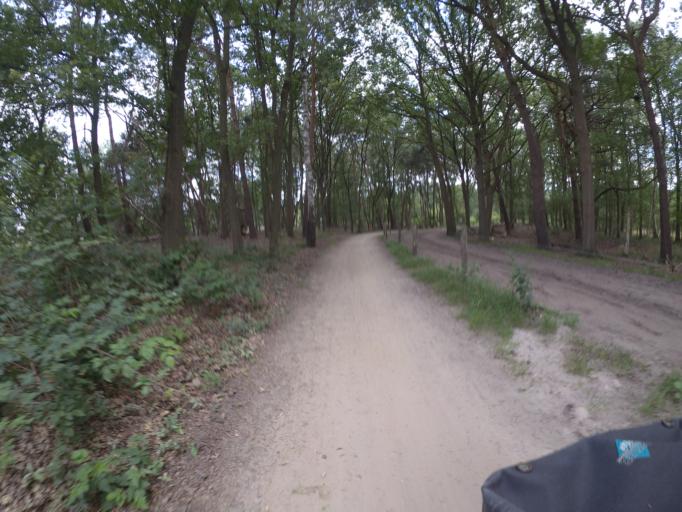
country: NL
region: North Brabant
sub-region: Gemeente Heeze-Leende
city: Heeze
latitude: 51.3995
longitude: 5.5878
